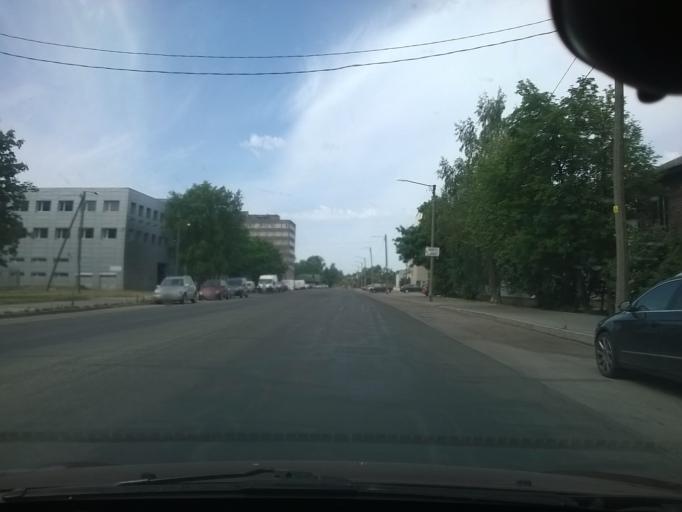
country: EE
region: Harju
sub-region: Tallinna linn
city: Tallinn
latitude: 59.4240
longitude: 24.6934
